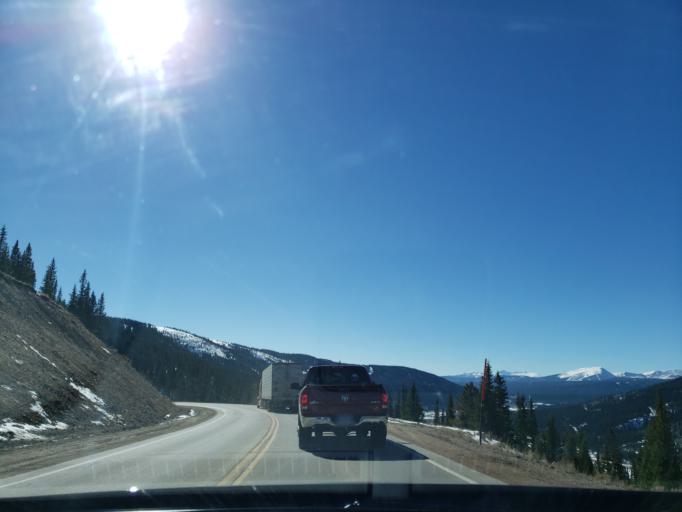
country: US
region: Colorado
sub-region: Summit County
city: Breckenridge
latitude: 39.3526
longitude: -106.0567
